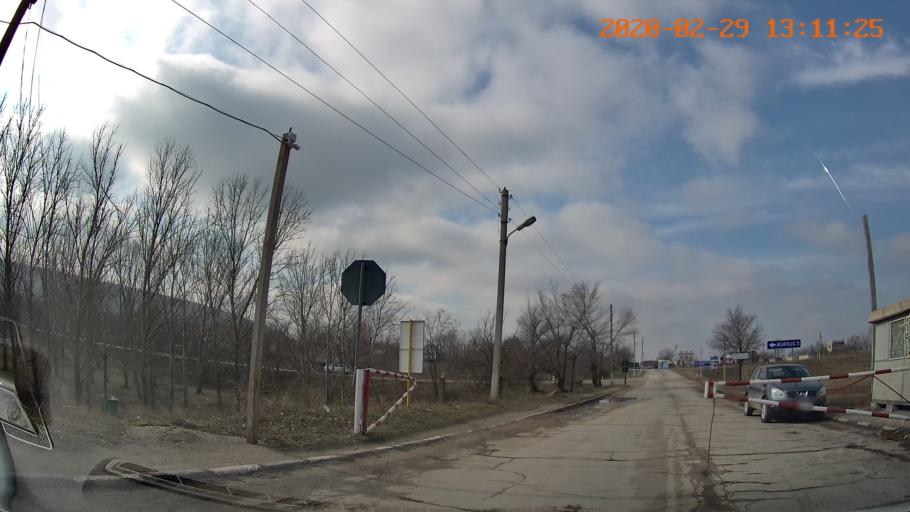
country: MD
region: Telenesti
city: Camenca
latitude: 48.0124
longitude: 28.6995
